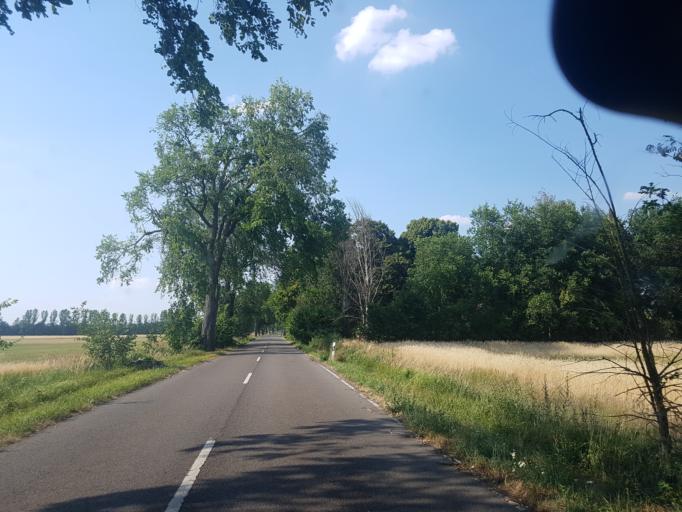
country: DE
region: Brandenburg
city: Trebbin
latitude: 52.1674
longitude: 13.2373
